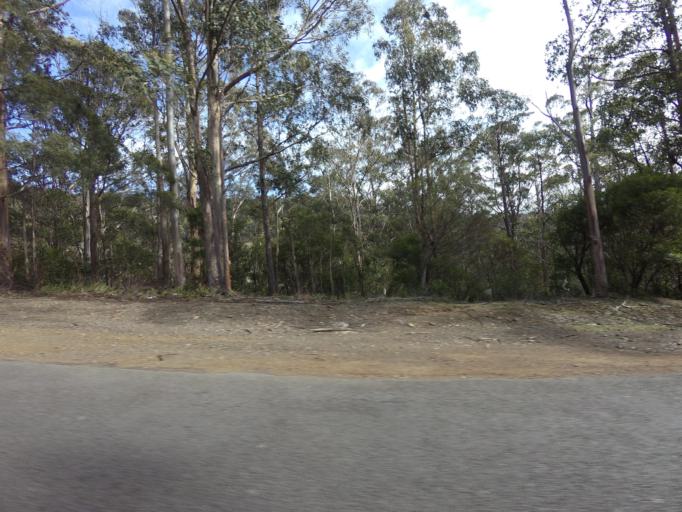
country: AU
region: Tasmania
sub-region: Kingborough
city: Margate
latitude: -43.0056
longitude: 147.1702
